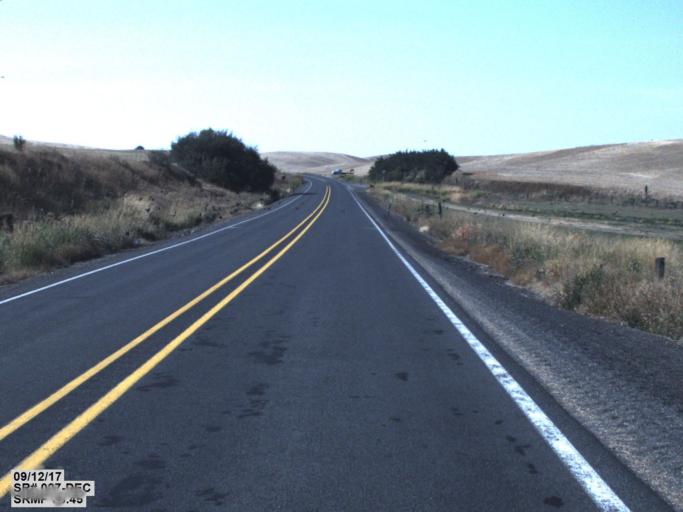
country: US
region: Washington
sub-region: Whitman County
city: Colfax
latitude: 47.1550
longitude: -117.2289
